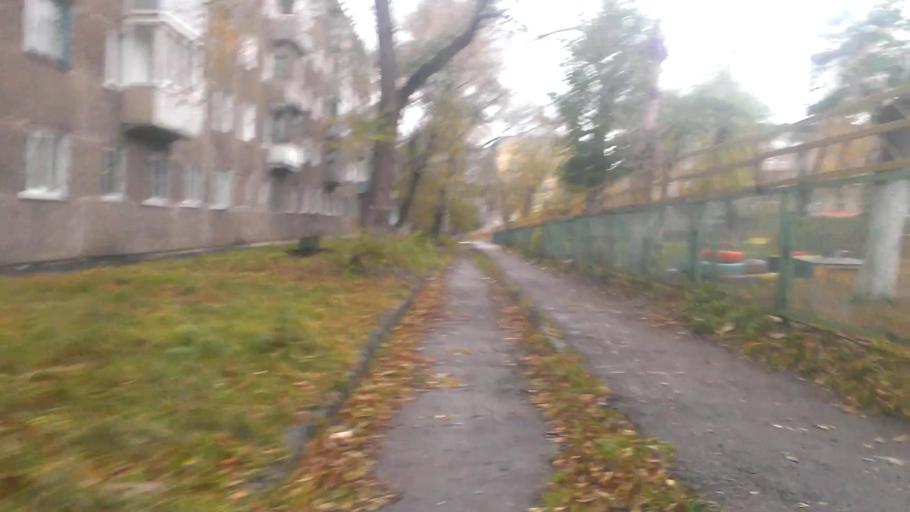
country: RU
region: Altai Krai
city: Novosilikatnyy
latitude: 53.3530
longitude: 83.6867
